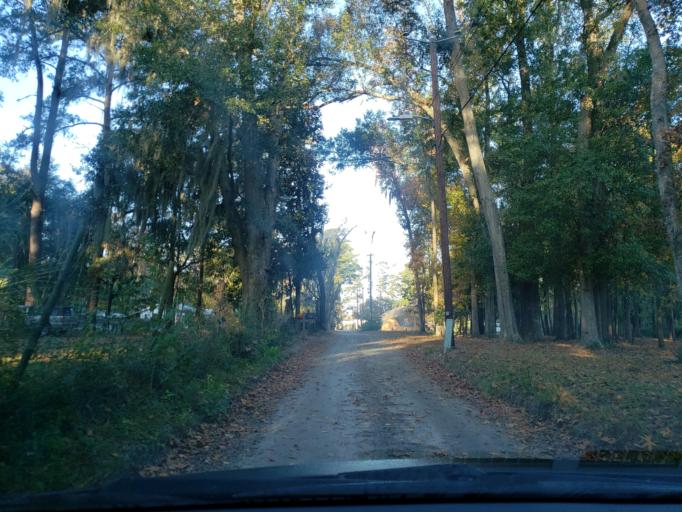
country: US
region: Georgia
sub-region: Chatham County
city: Montgomery
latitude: 31.9825
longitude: -81.1273
